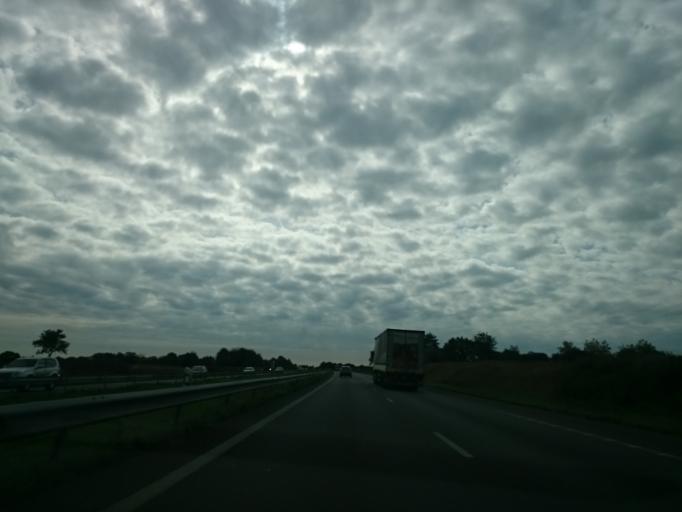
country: FR
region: Pays de la Loire
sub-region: Departement de la Loire-Atlantique
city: Le Temple-de-Bretagne
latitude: 47.3139
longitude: -1.7694
